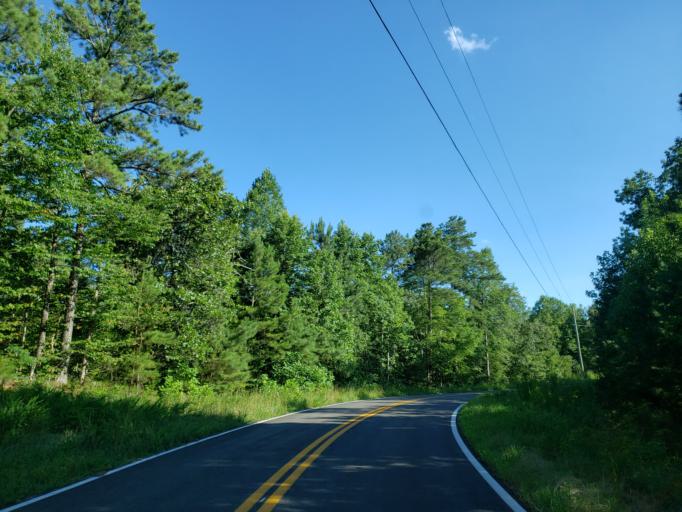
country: US
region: Georgia
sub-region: Bartow County
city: Rydal
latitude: 34.3671
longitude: -84.6191
